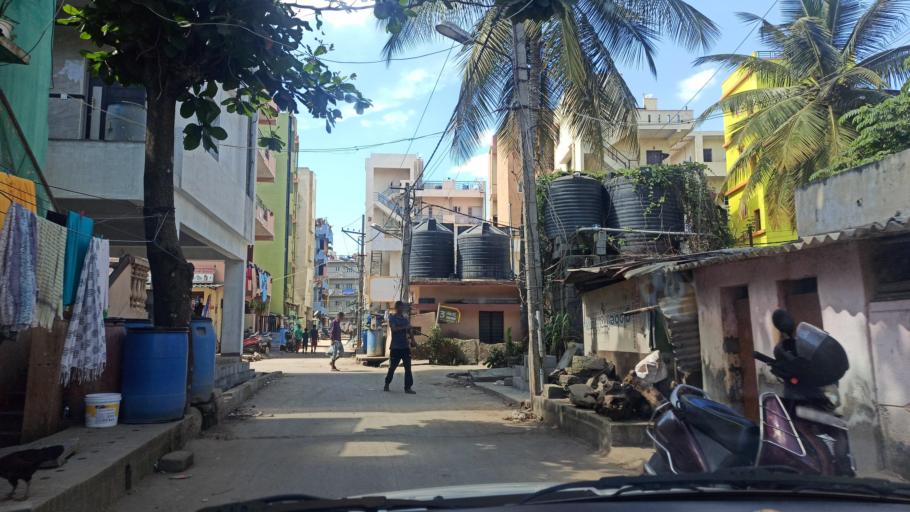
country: IN
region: Karnataka
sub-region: Bangalore Urban
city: Bangalore
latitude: 12.9231
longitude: 77.6633
